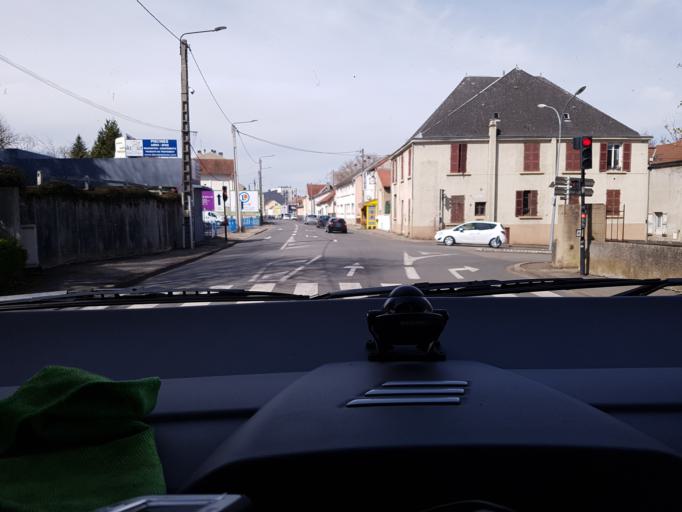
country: FR
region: Auvergne
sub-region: Departement de l'Allier
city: Cusset
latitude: 46.1344
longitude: 3.4461
